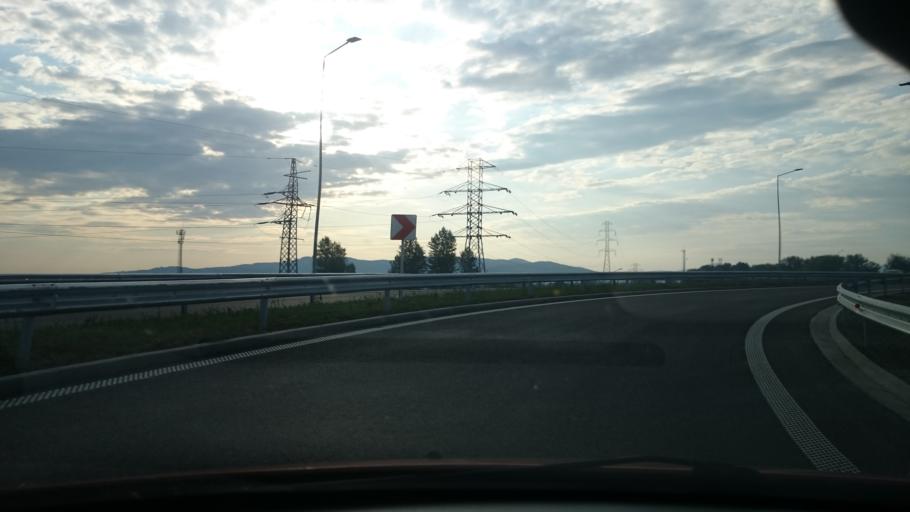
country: PL
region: Lower Silesian Voivodeship
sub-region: Powiat klodzki
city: Klodzko
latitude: 50.4408
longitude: 16.6244
